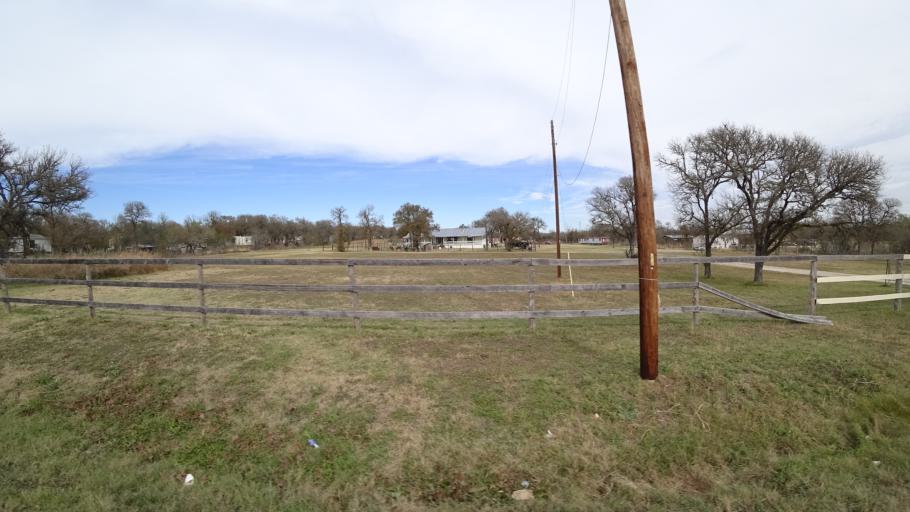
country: US
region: Texas
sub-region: Travis County
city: Garfield
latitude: 30.1333
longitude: -97.5755
